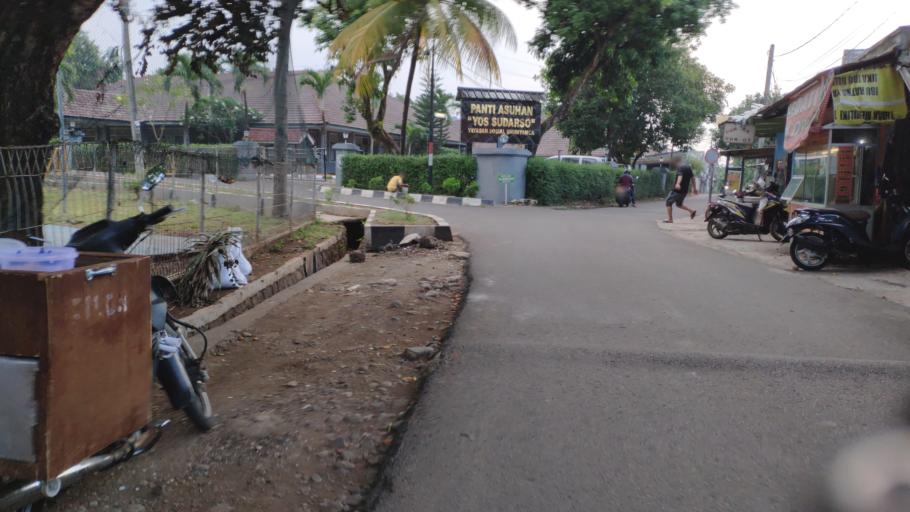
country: ID
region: West Java
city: Pamulang
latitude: -6.2980
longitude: 106.8087
